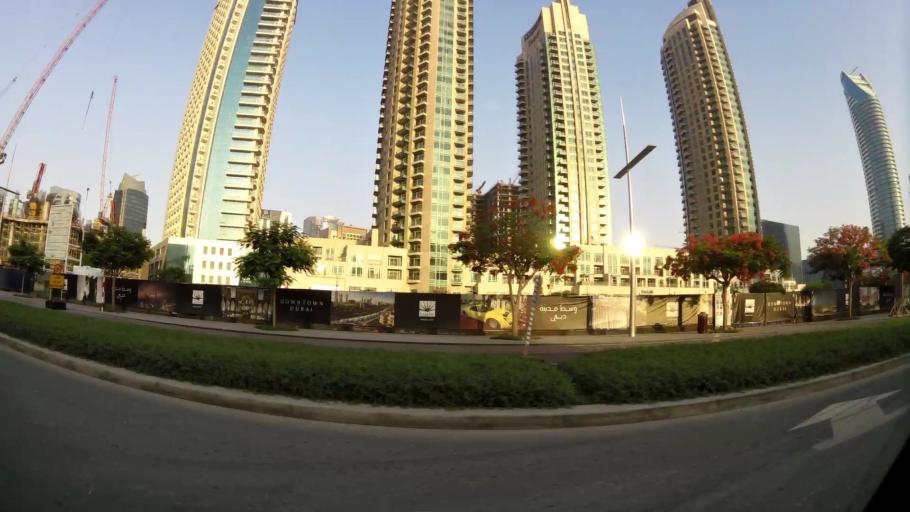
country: AE
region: Dubai
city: Dubai
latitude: 25.1914
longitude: 55.2805
